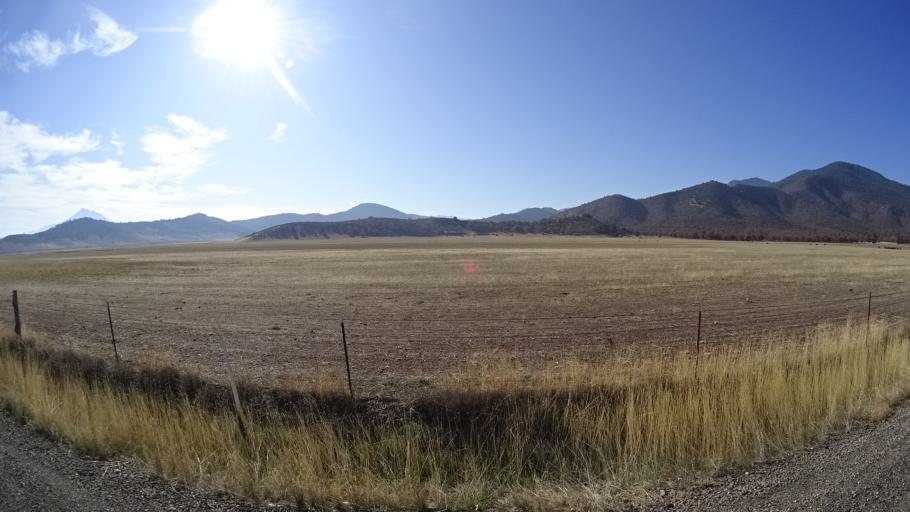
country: US
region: California
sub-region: Siskiyou County
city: Montague
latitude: 41.6552
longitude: -122.5739
